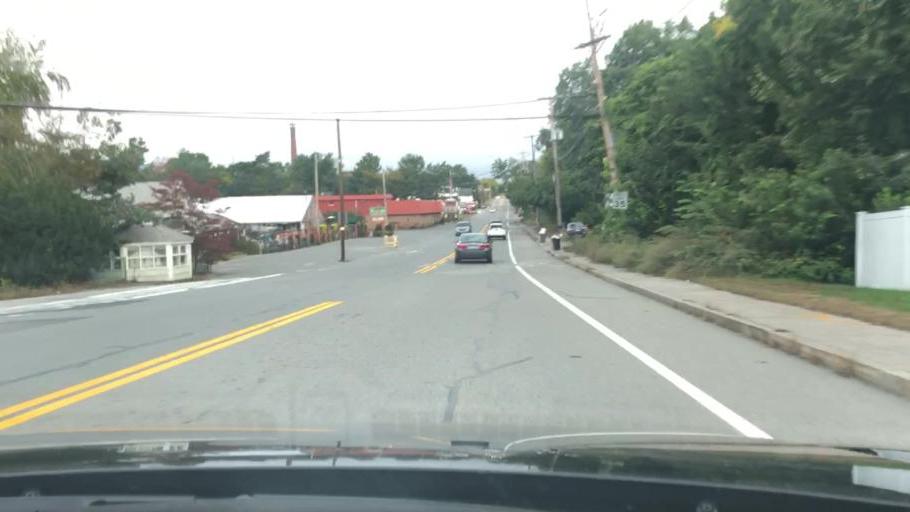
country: US
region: Massachusetts
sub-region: Middlesex County
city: Chelmsford
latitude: 42.6322
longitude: -71.3751
